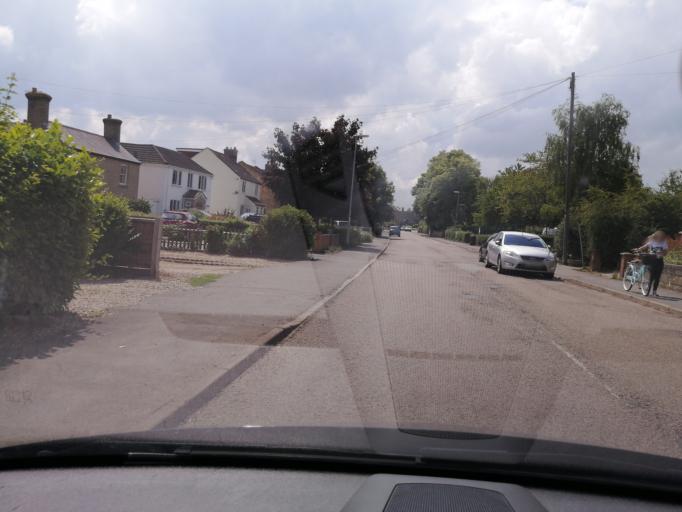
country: GB
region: England
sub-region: Cambridgeshire
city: Yaxley
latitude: 52.5147
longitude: -0.2513
